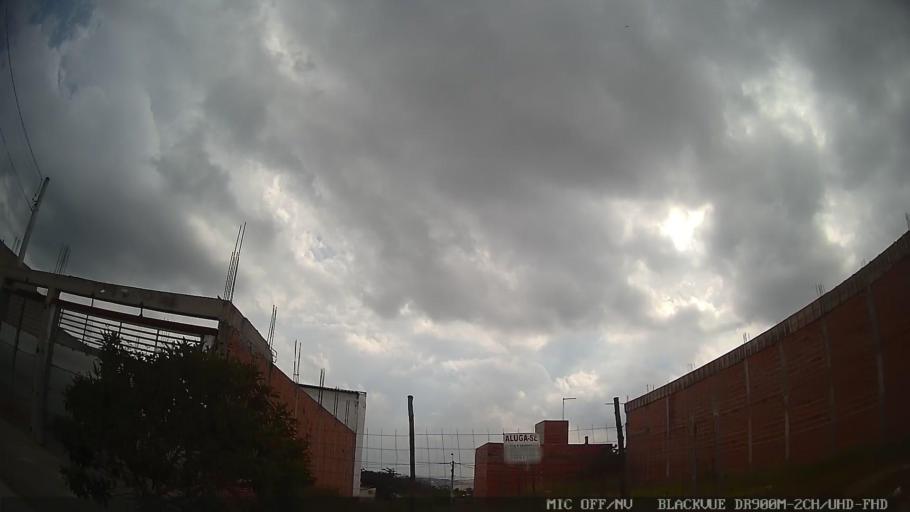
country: BR
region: Sao Paulo
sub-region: Indaiatuba
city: Indaiatuba
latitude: -23.1234
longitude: -47.2532
